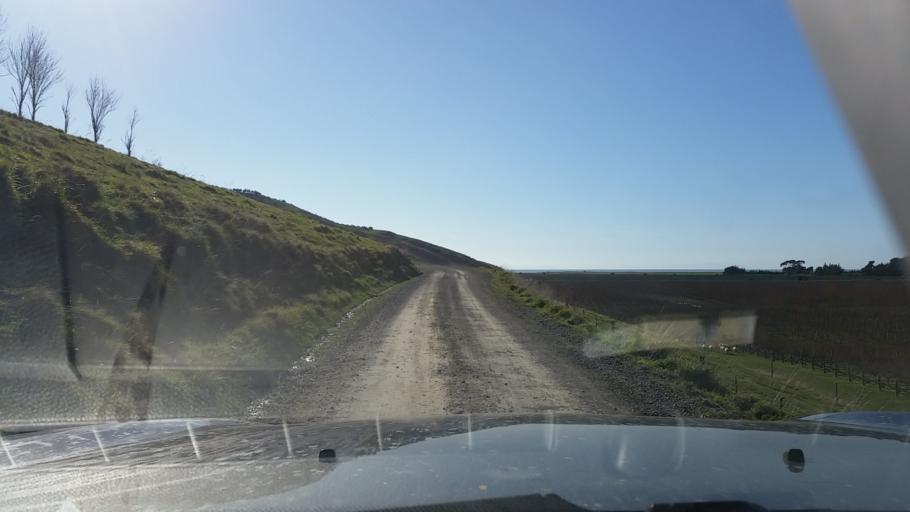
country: NZ
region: Marlborough
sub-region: Marlborough District
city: Blenheim
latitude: -41.6682
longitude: 174.1406
